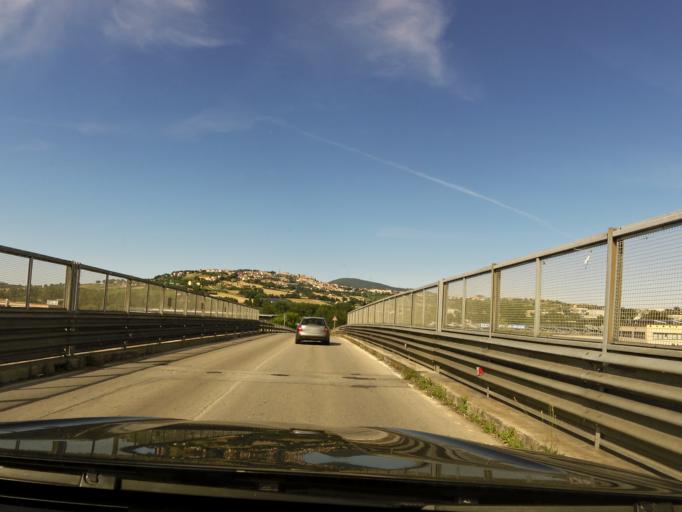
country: IT
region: The Marches
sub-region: Provincia di Ancona
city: Camerano
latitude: 43.5148
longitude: 13.5274
